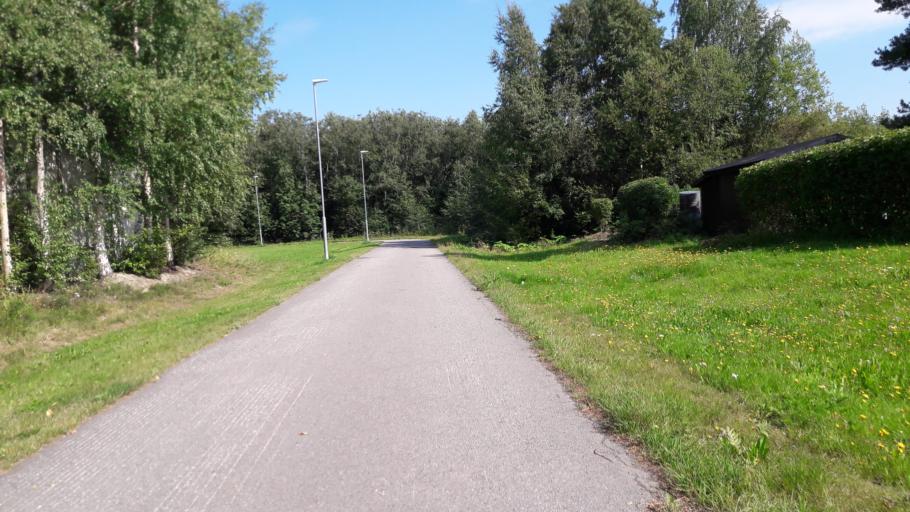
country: FI
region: North Karelia
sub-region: Joensuu
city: Joensuu
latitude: 62.5502
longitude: 29.8331
